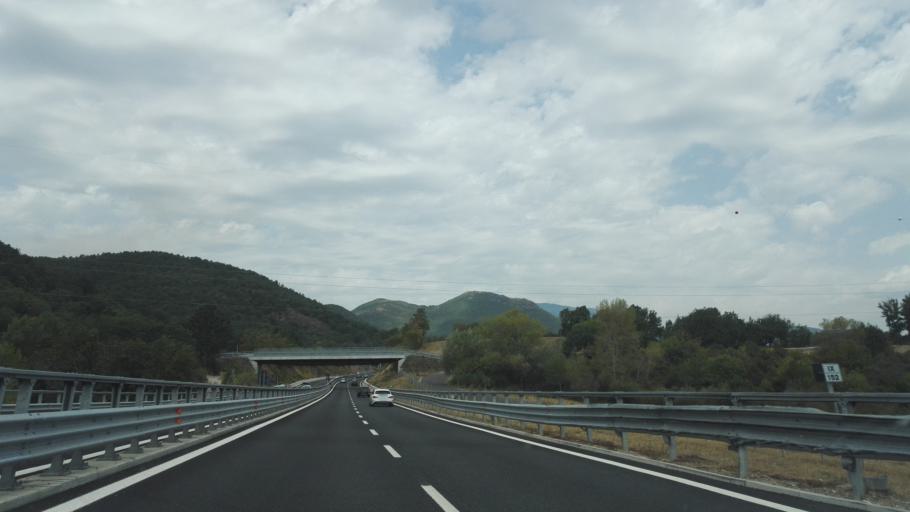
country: IT
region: Calabria
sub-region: Provincia di Cosenza
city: Laino Borgo
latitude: 39.9615
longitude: 15.9332
